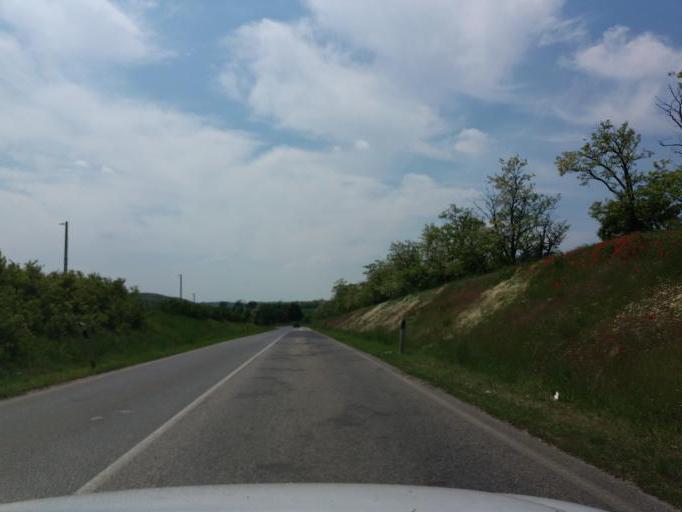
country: HU
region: Pest
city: Soskut
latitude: 47.3828
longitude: 18.8010
